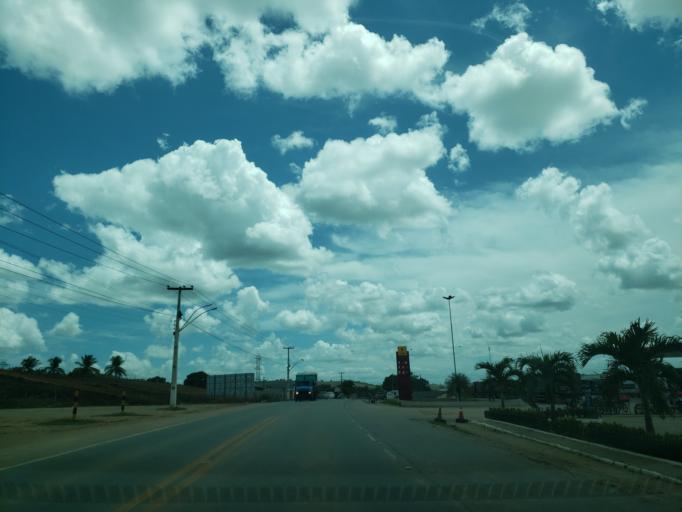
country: BR
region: Alagoas
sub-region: Uniao Dos Palmares
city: Uniao dos Palmares
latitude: -9.1573
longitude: -36.0137
